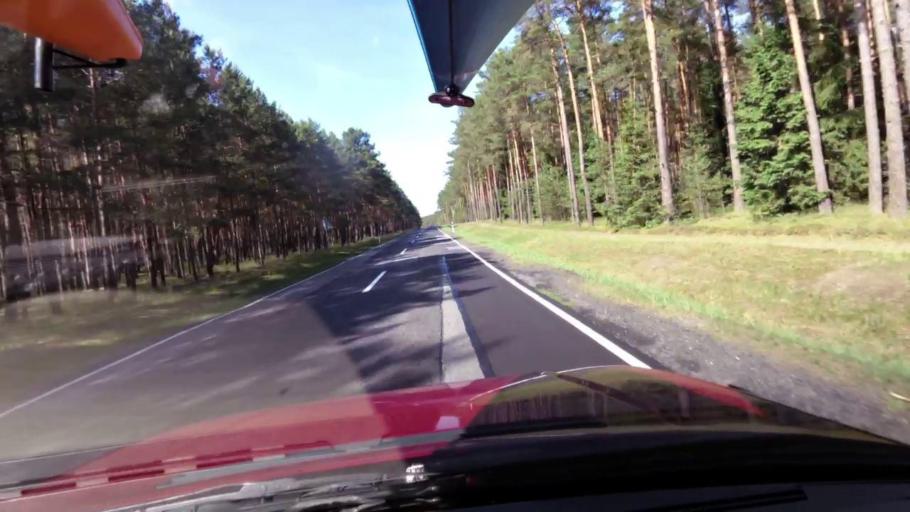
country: PL
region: Pomeranian Voivodeship
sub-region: Powiat bytowski
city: Trzebielino
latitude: 54.1672
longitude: 17.0601
